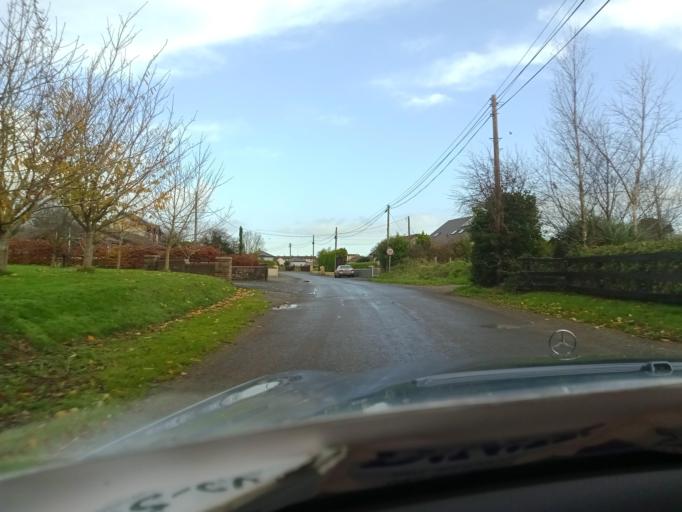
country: IE
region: Leinster
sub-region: Kilkenny
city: Mooncoin
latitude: 52.2884
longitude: -7.2522
